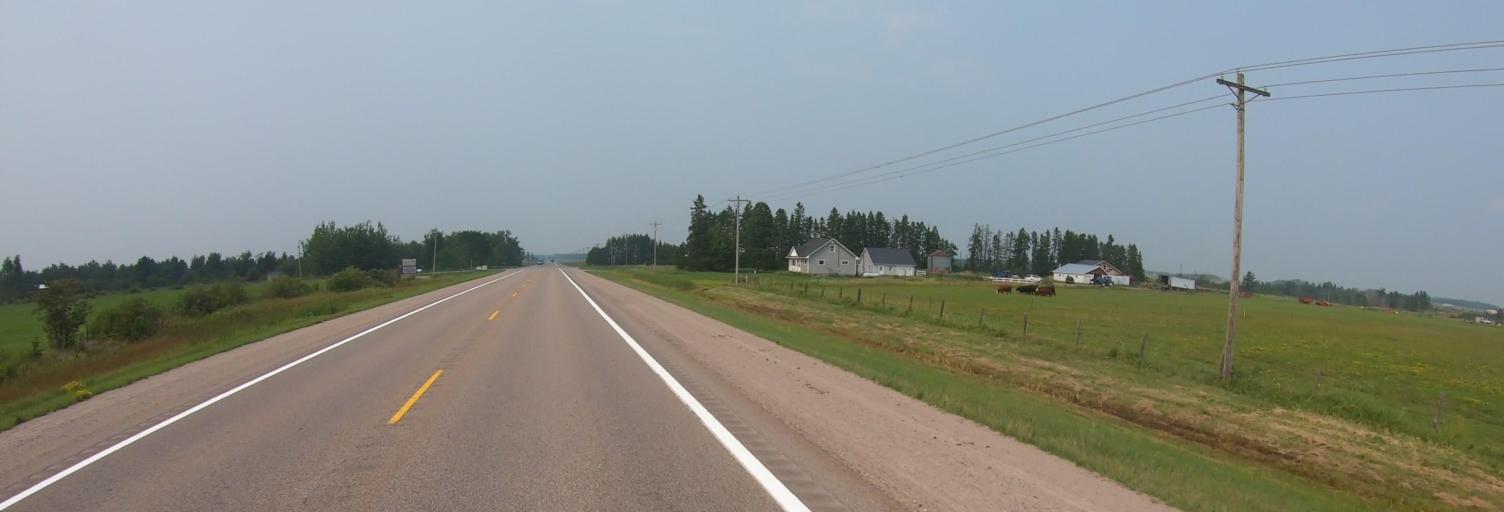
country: US
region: Michigan
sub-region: Chippewa County
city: Sault Ste. Marie
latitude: 46.3448
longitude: -84.3639
